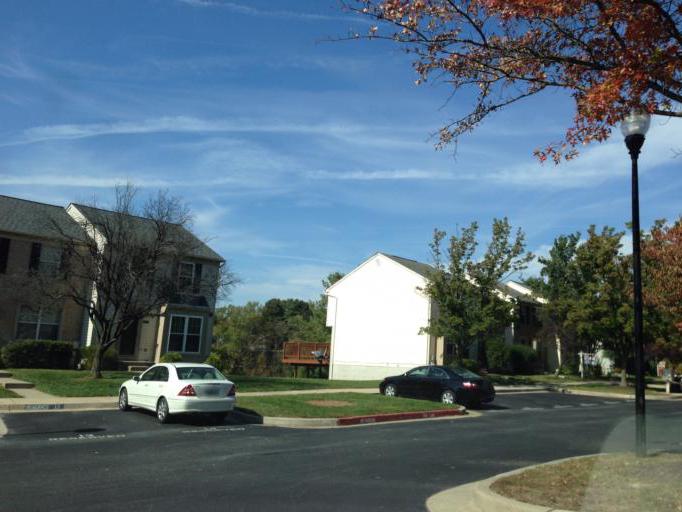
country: US
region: Maryland
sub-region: Howard County
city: Ellicott City
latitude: 39.2617
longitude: -76.8179
